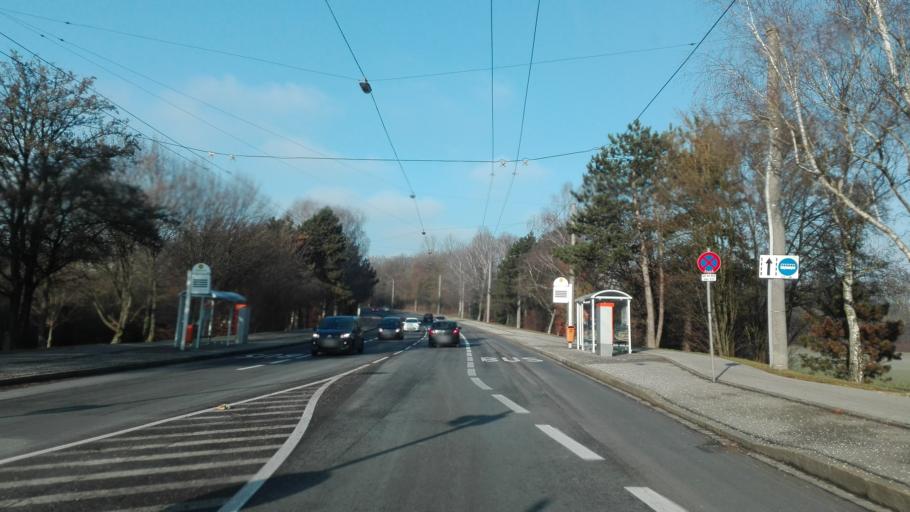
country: AT
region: Upper Austria
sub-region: Politischer Bezirk Linz-Land
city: Leonding
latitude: 48.2619
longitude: 14.2901
